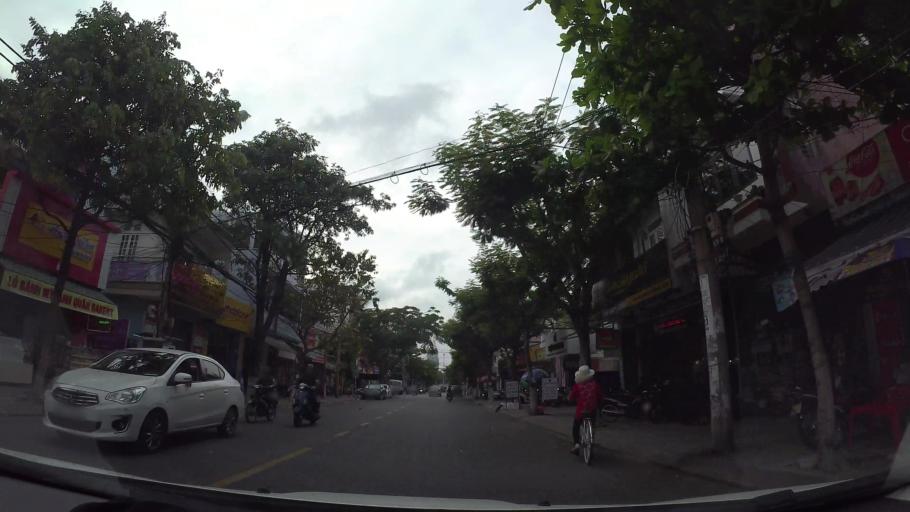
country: VN
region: Da Nang
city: Son Tra
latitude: 16.0669
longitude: 108.2354
